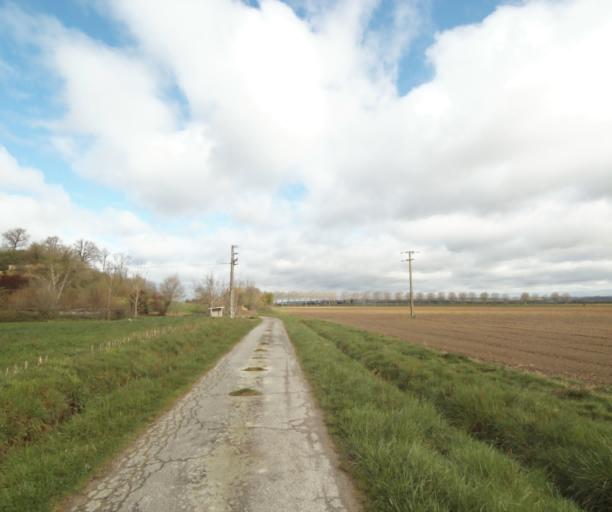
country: FR
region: Midi-Pyrenees
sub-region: Departement de l'Ariege
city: Saverdun
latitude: 43.2461
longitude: 1.5472
